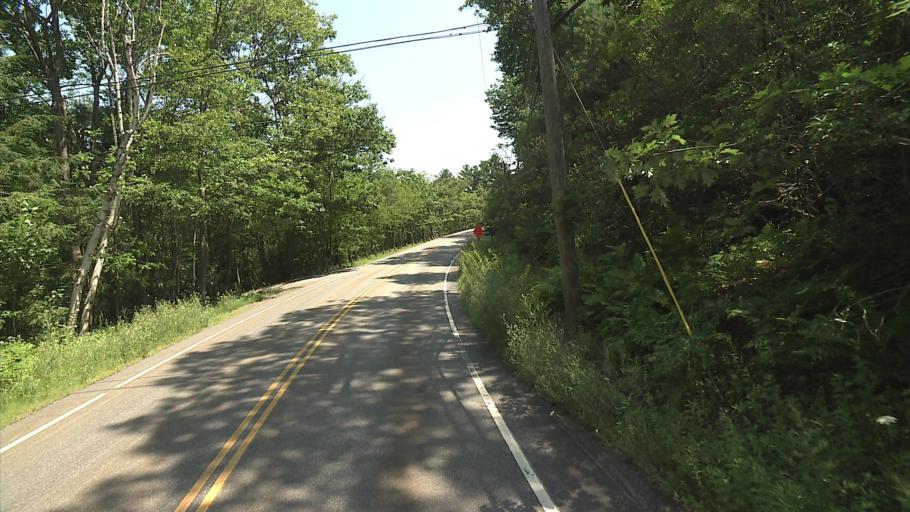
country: US
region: Connecticut
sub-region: Litchfield County
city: Winchester Center
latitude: 41.9158
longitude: -73.1110
